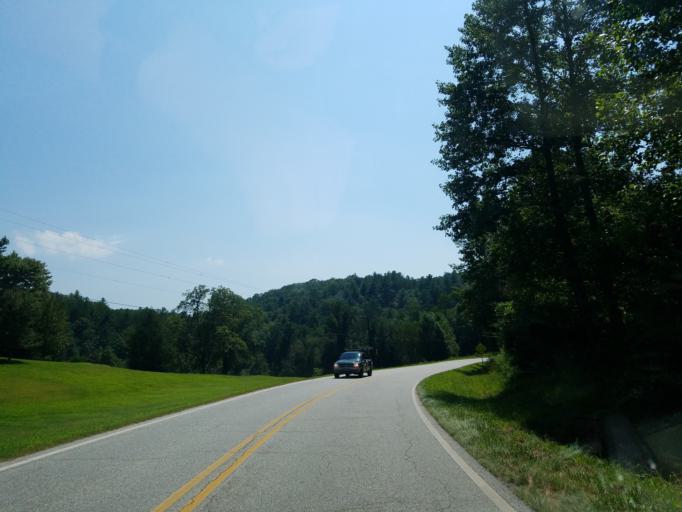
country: US
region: Georgia
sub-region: Lumpkin County
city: Dahlonega
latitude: 34.6331
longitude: -83.9176
